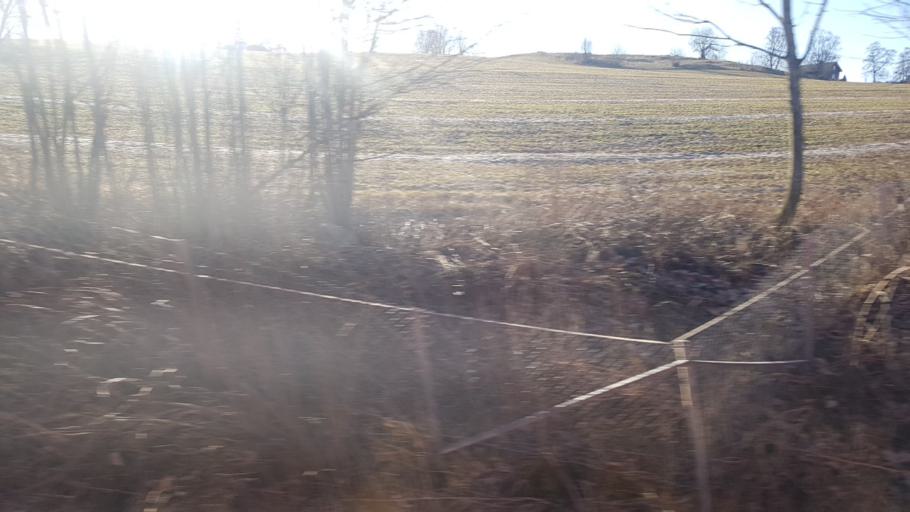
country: NO
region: Nord-Trondelag
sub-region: Levanger
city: Levanger
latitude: 63.7262
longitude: 11.2622
